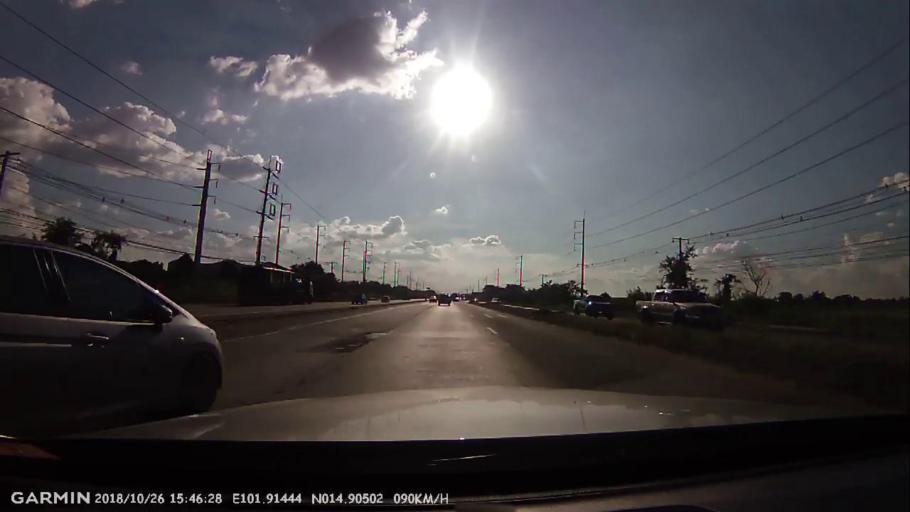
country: TH
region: Nakhon Ratchasima
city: Kham Thale So
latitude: 14.9049
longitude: 101.9144
